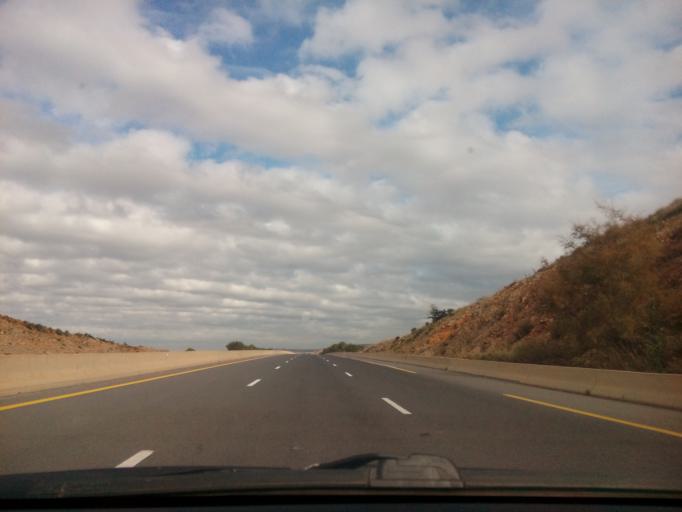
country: DZ
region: Tlemcen
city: Chetouane
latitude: 34.9447
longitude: -1.3088
